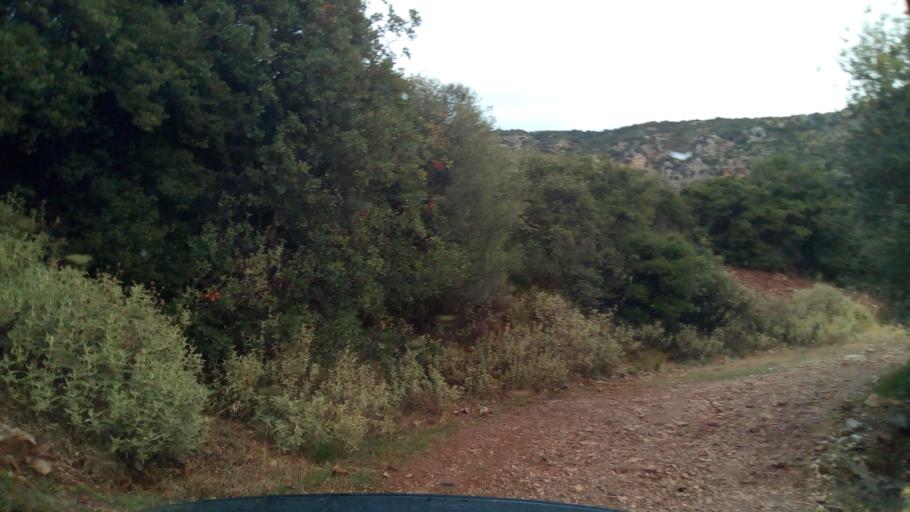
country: GR
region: West Greece
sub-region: Nomos Achaias
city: Kamarai
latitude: 38.4139
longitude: 22.0545
